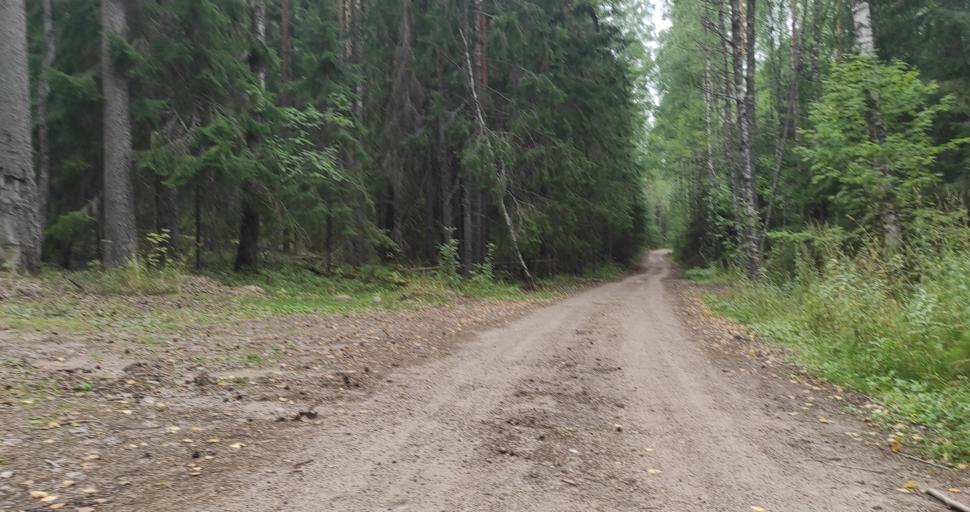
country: RU
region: Leningrad
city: Veshchevo
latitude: 60.6863
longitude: 29.2472
